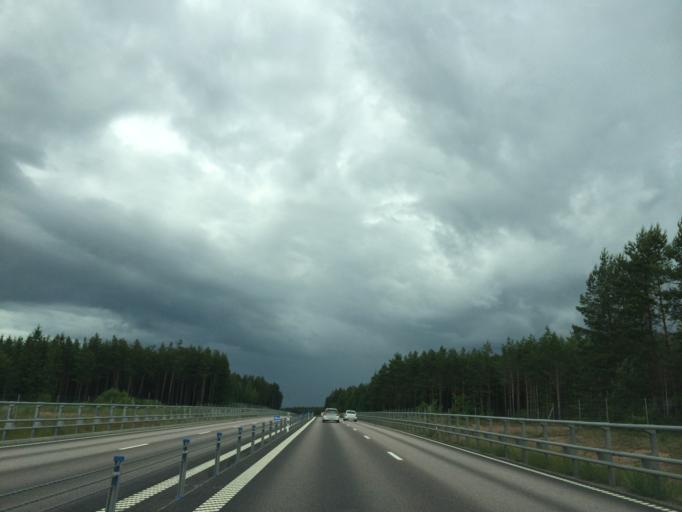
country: SE
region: OEstergoetland
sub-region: Mjolby Kommun
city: Mjolby
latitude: 58.3499
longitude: 15.1080
